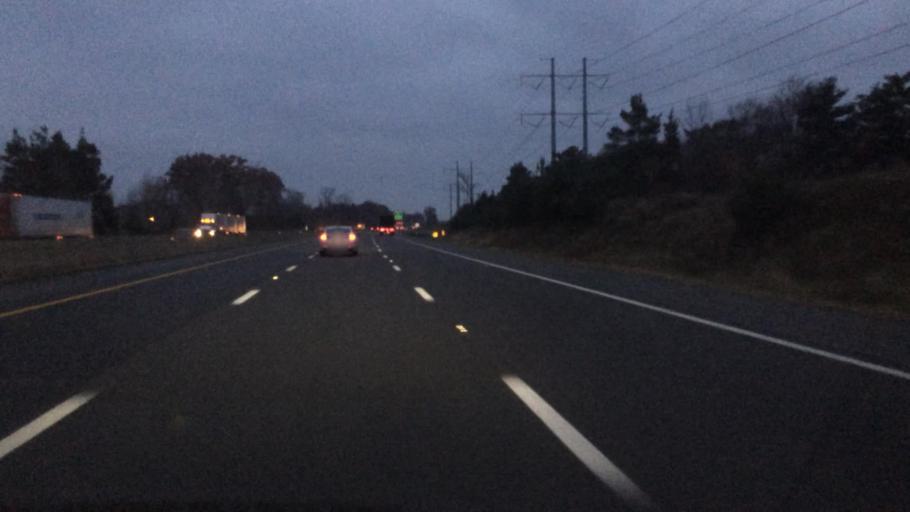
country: US
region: Ohio
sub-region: Cuyahoga County
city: North Royalton
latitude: 41.3190
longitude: -81.7752
